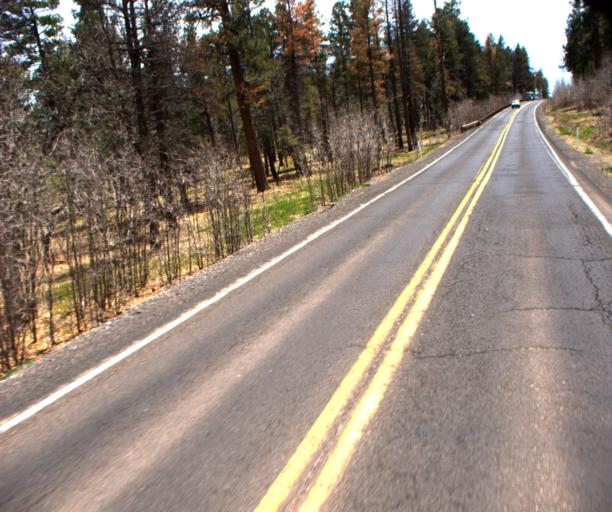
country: US
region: Arizona
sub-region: Coconino County
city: Kachina Village
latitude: 35.0614
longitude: -111.7326
